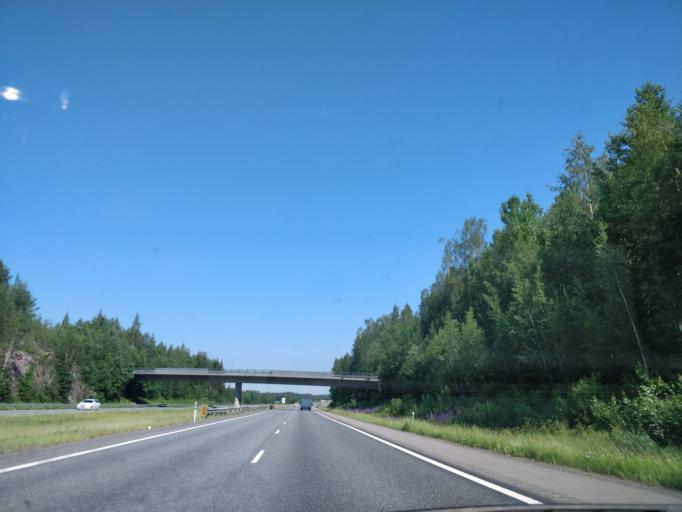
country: FI
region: Haeme
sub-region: Riihimaeki
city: Riihimaeki
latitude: 60.7644
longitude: 24.7222
